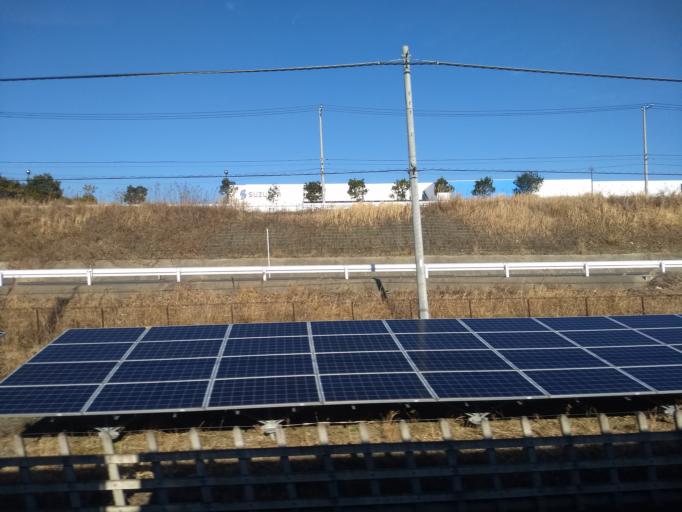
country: JP
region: Chiba
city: Sakura
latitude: 35.7970
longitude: 140.1814
